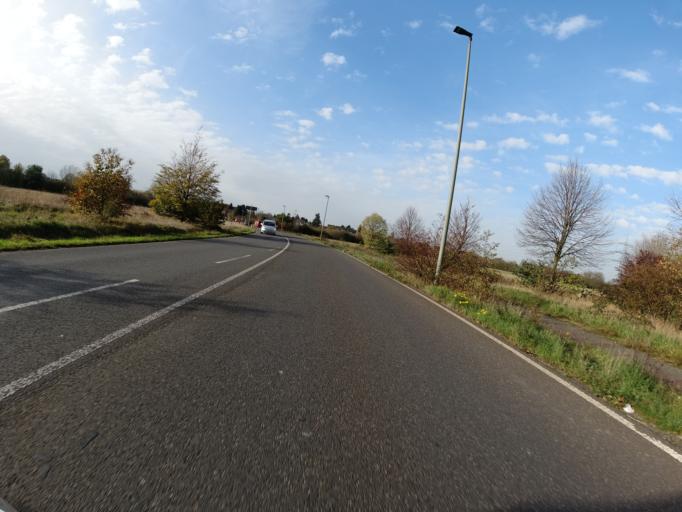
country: DE
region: North Rhine-Westphalia
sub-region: Regierungsbezirk Dusseldorf
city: Hochfeld
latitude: 51.3868
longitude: 6.6884
